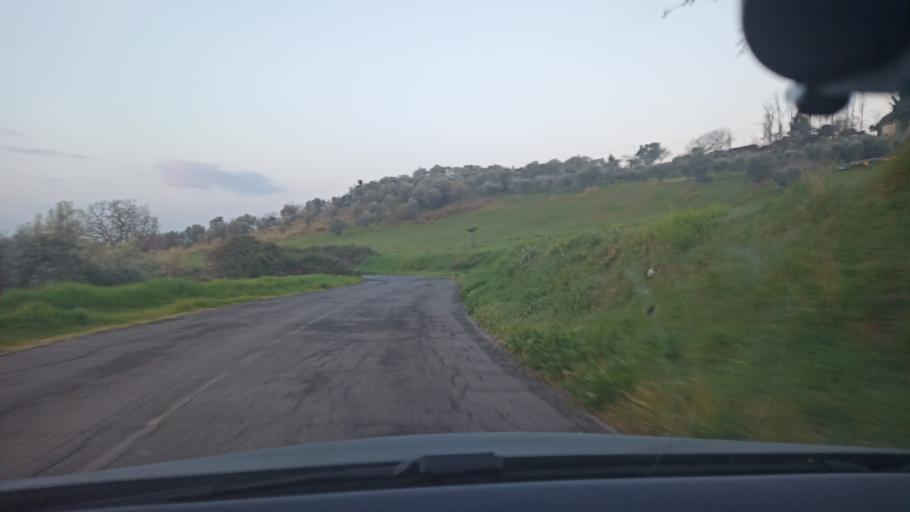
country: IT
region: Latium
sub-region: Provincia di Rieti
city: Torri in Sabina
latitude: 42.3634
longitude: 12.6549
